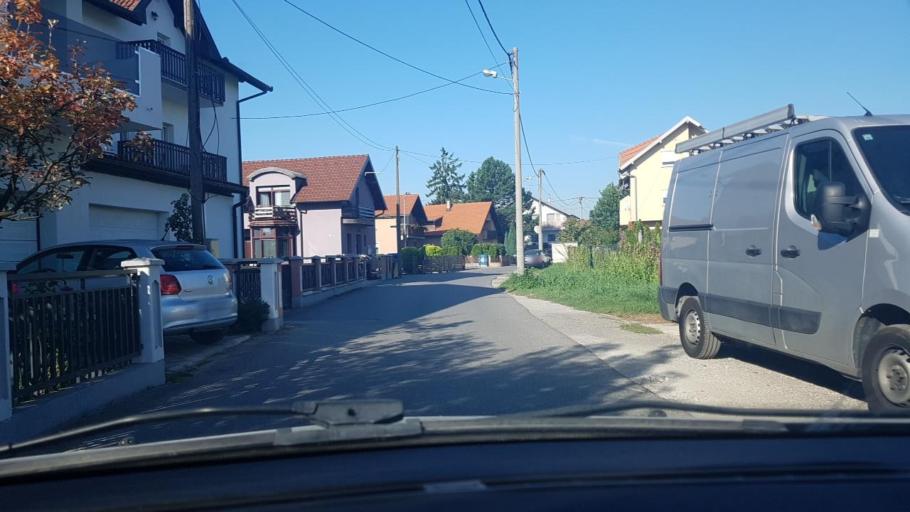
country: HR
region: Grad Zagreb
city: Novi Zagreb
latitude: 45.7604
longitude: 15.9657
